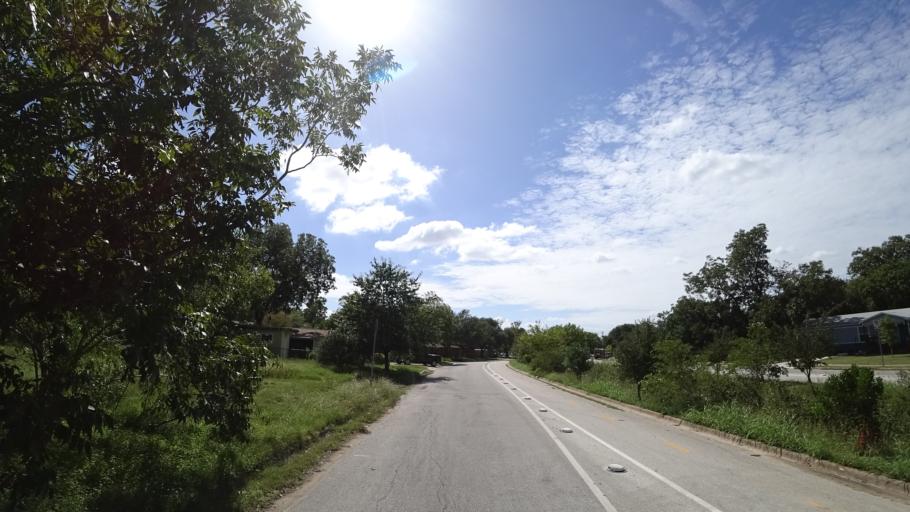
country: US
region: Texas
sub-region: Travis County
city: Austin
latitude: 30.3412
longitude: -97.7283
